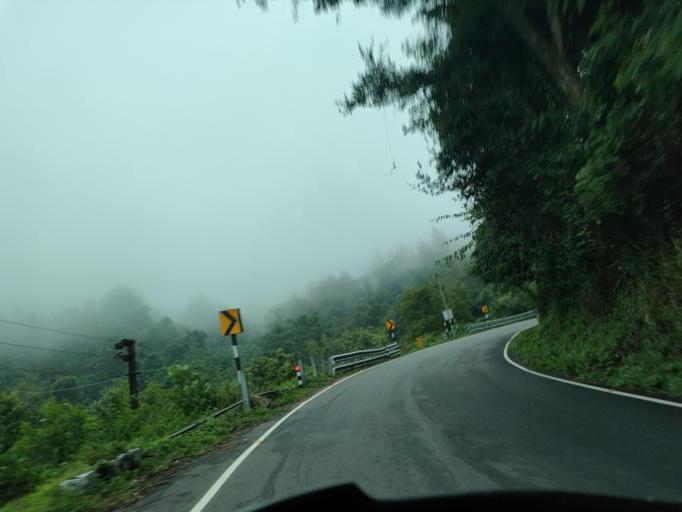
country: IN
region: Tamil Nadu
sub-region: Dindigul
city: Ayakudi
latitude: 10.3552
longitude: 77.5603
